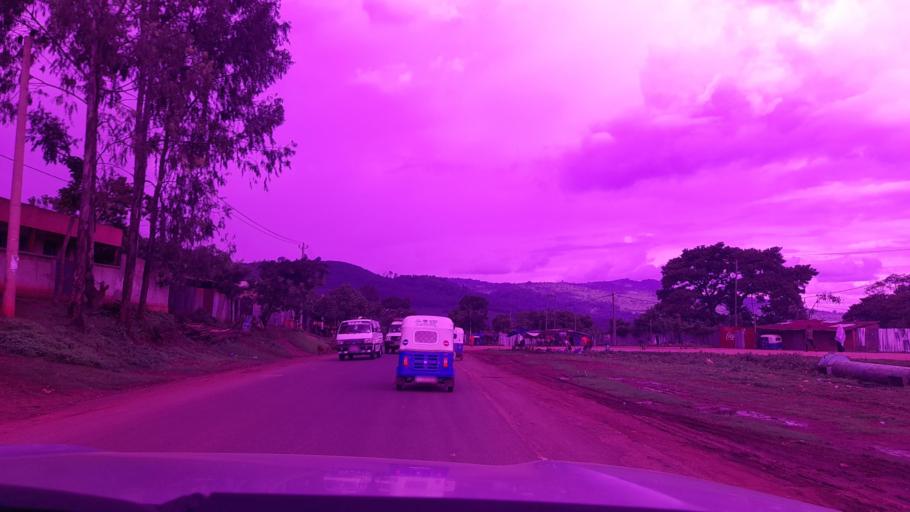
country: ET
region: Oromiya
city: Jima
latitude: 7.6699
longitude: 36.8585
